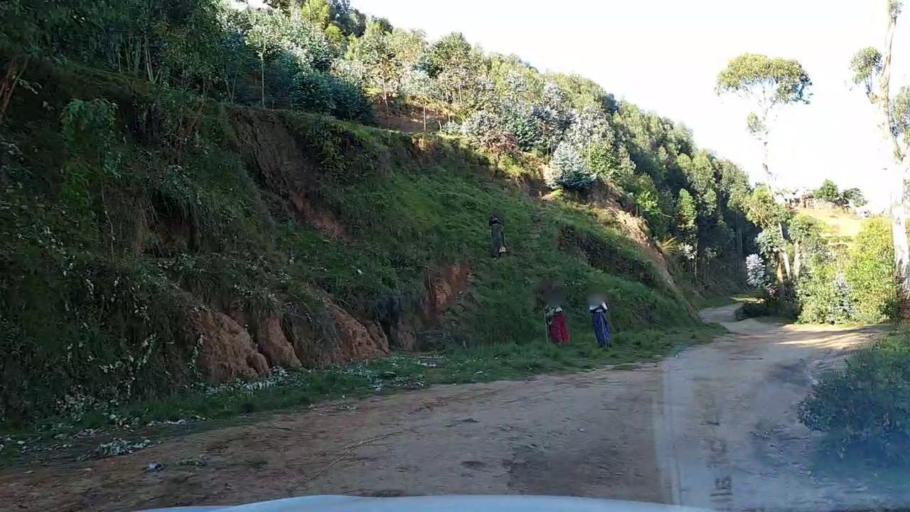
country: RW
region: Southern Province
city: Gikongoro
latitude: -2.4128
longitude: 29.5190
